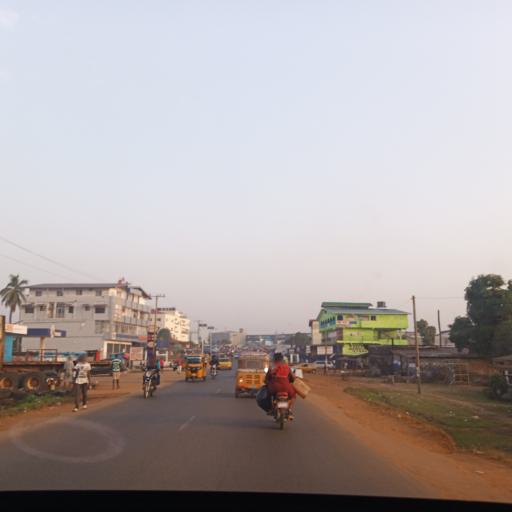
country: LR
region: Montserrado
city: Monrovia
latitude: 6.2619
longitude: -10.7040
